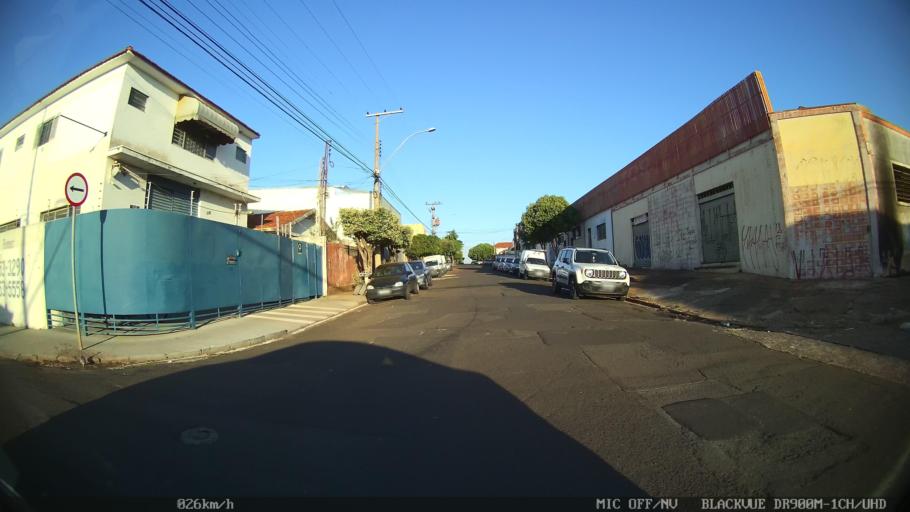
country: BR
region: Sao Paulo
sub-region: Sao Jose Do Rio Preto
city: Sao Jose do Rio Preto
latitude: -20.7961
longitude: -49.3889
